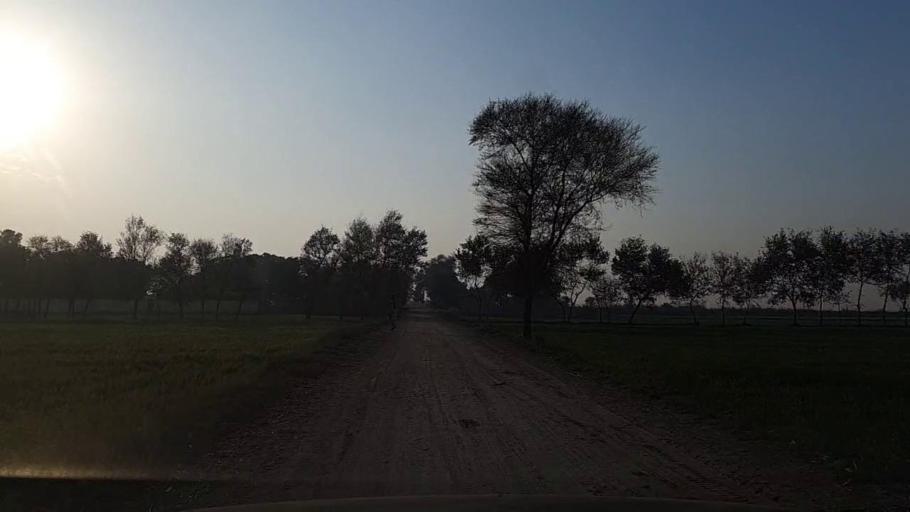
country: PK
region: Sindh
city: Daur
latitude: 26.4695
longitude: 68.3825
